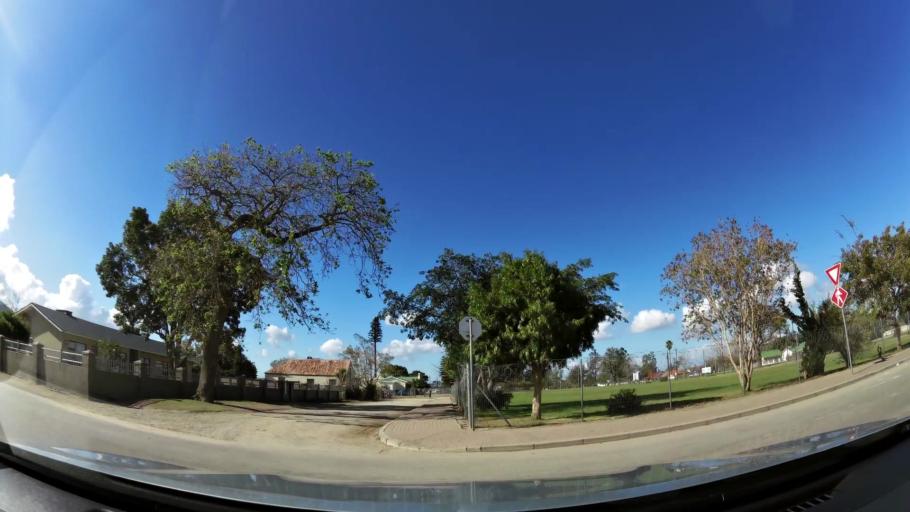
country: ZA
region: Western Cape
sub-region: Eden District Municipality
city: George
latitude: -33.9453
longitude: 22.4172
